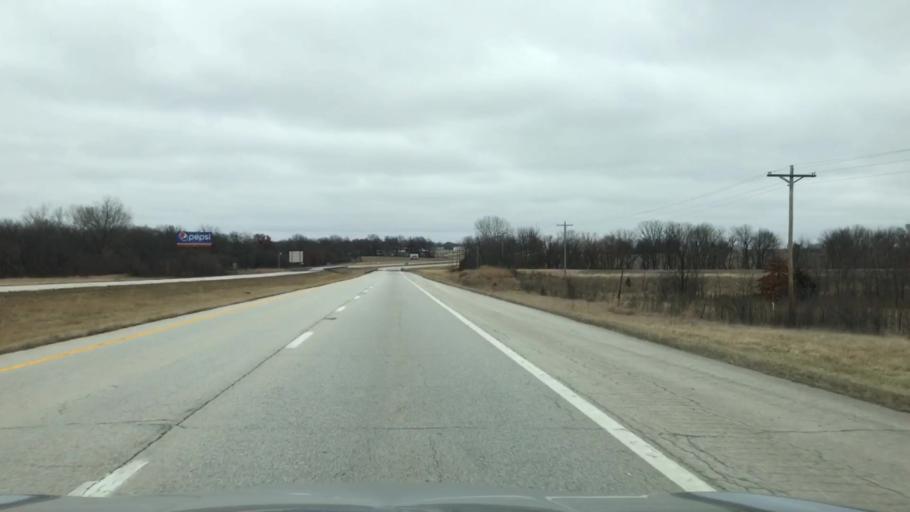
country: US
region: Missouri
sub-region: Livingston County
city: Chillicothe
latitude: 39.7741
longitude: -93.5343
